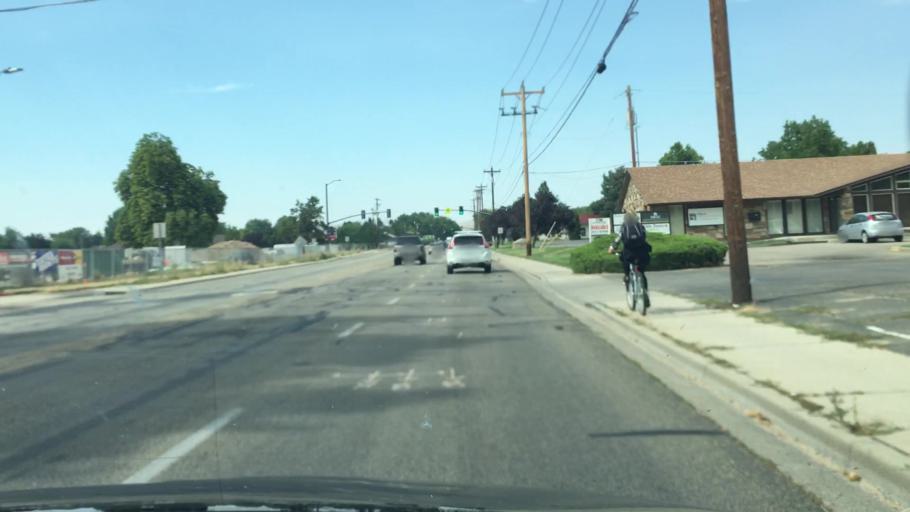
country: US
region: Idaho
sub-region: Ada County
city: Garden City
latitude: 43.6238
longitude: -116.2742
